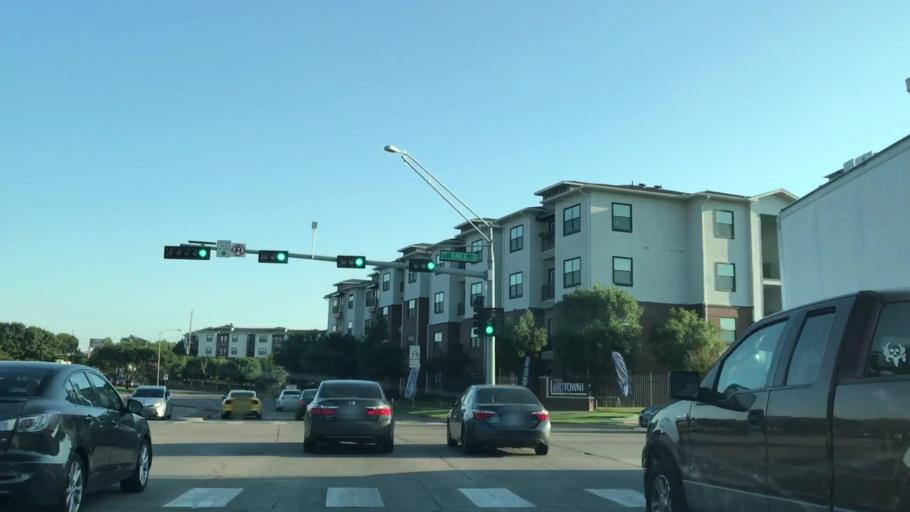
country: US
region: Texas
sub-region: Denton County
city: Denton
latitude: 33.2067
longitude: -97.1367
